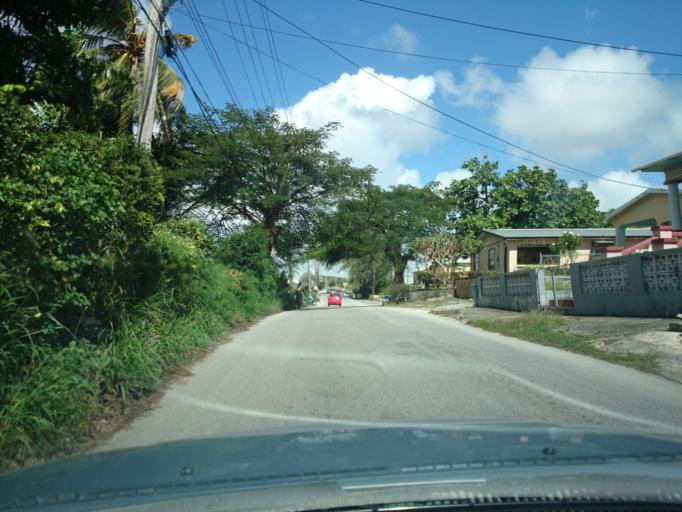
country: BB
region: Christ Church
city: Oistins
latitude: 13.0765
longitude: -59.5585
